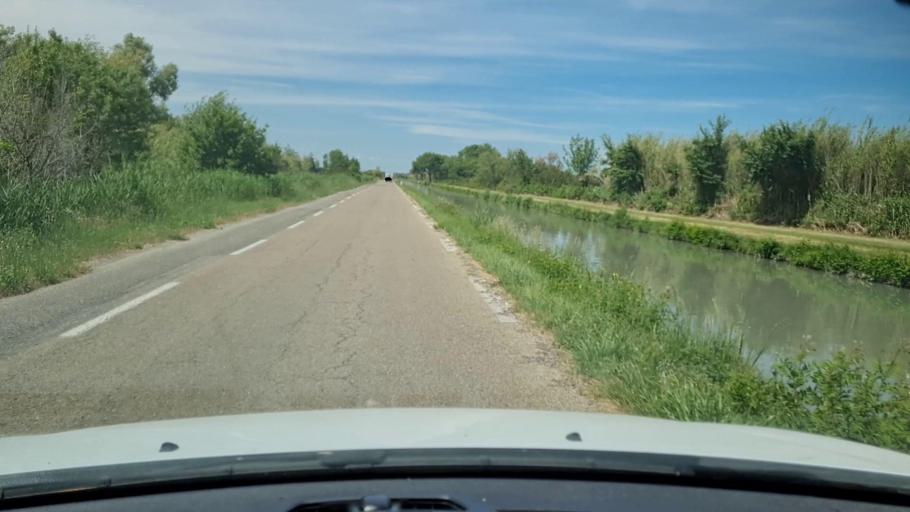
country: FR
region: Languedoc-Roussillon
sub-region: Departement du Gard
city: Saint-Gilles
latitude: 43.5897
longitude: 4.3445
